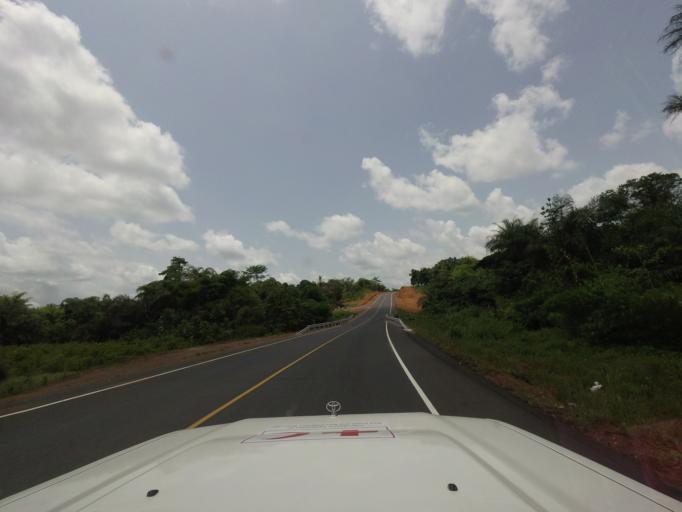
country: LR
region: Margibi
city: Kakata
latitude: 6.4653
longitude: -10.4180
